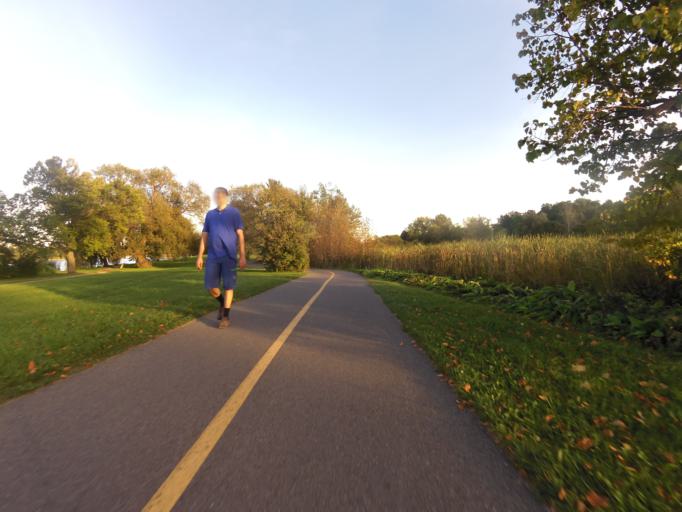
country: CA
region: Ontario
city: Ottawa
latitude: 45.3945
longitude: -75.7047
